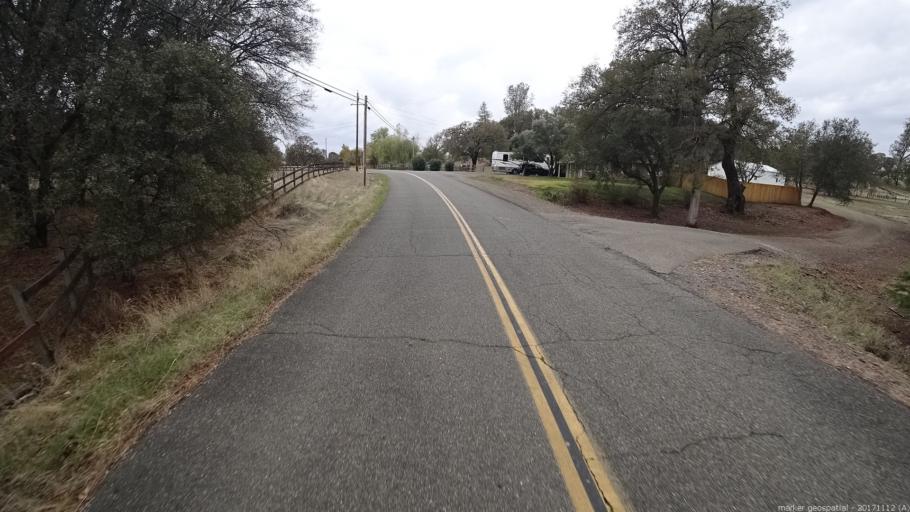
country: US
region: California
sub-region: Shasta County
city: Palo Cedro
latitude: 40.5397
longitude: -122.2276
